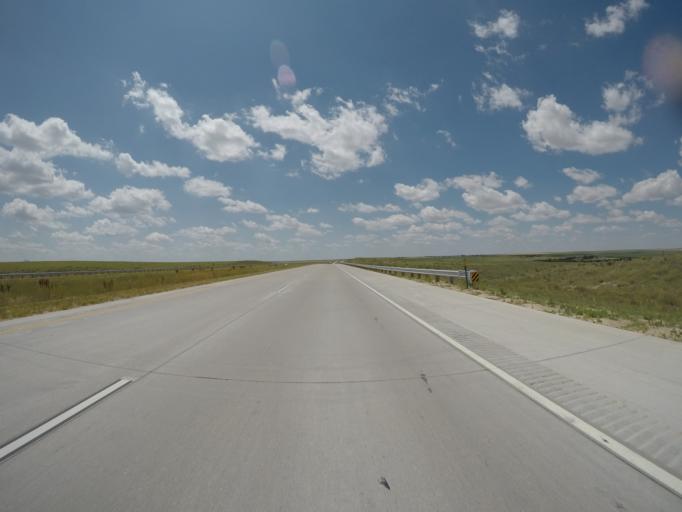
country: US
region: Colorado
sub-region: Kit Carson County
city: Burlington
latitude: 39.2943
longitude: -102.6385
